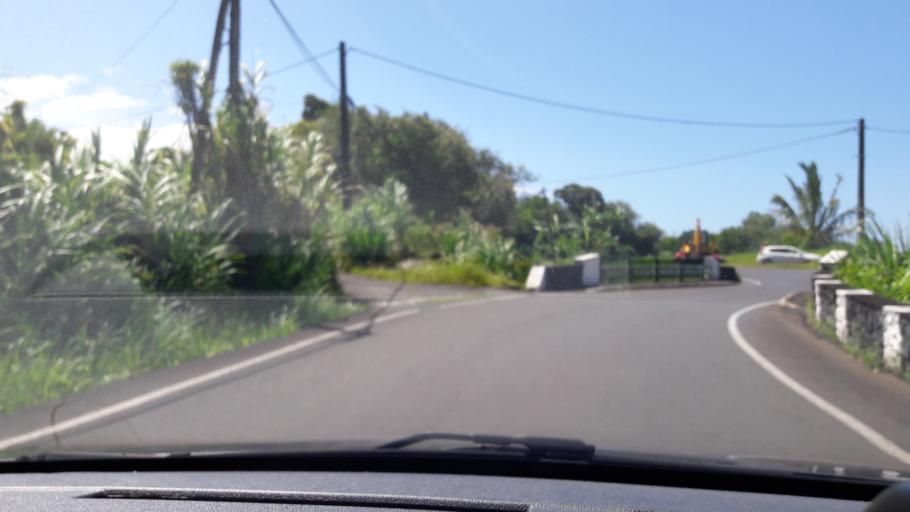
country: RE
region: Reunion
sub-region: Reunion
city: Saint-Benoit
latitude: -21.0914
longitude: 55.7028
